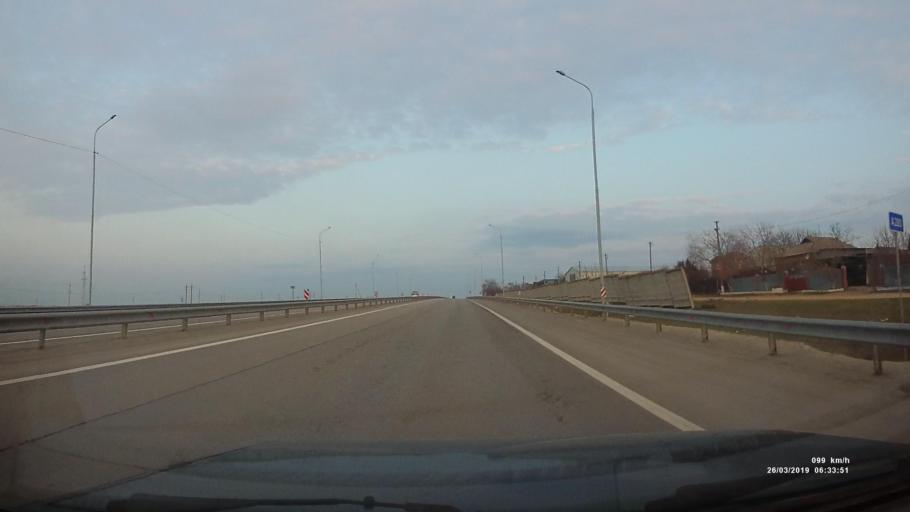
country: RU
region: Rostov
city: Chaltyr
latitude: 47.2751
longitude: 39.4800
